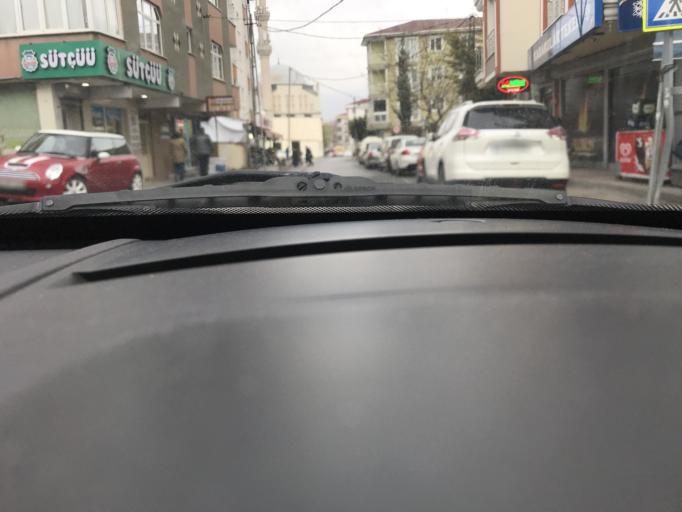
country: TR
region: Istanbul
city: Yakuplu
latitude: 41.0031
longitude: 28.6946
